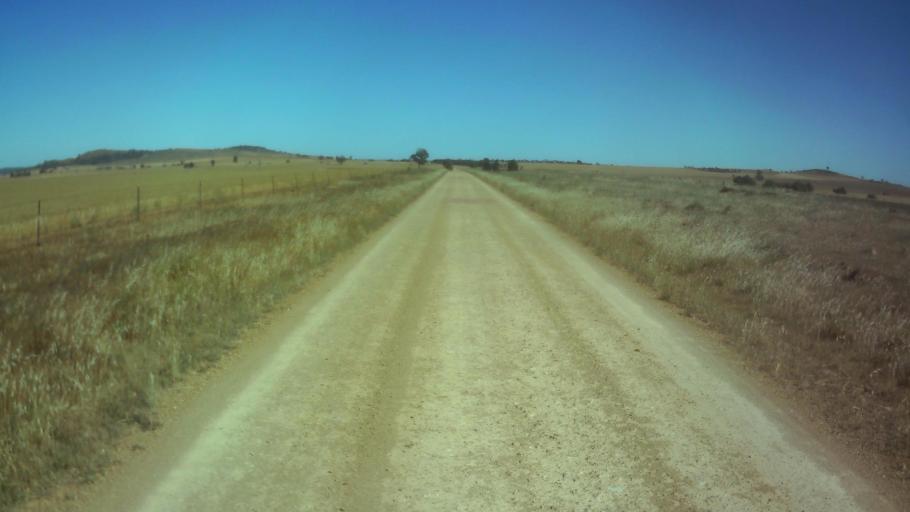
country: AU
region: New South Wales
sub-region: Weddin
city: Grenfell
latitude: -33.9786
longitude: 148.3260
